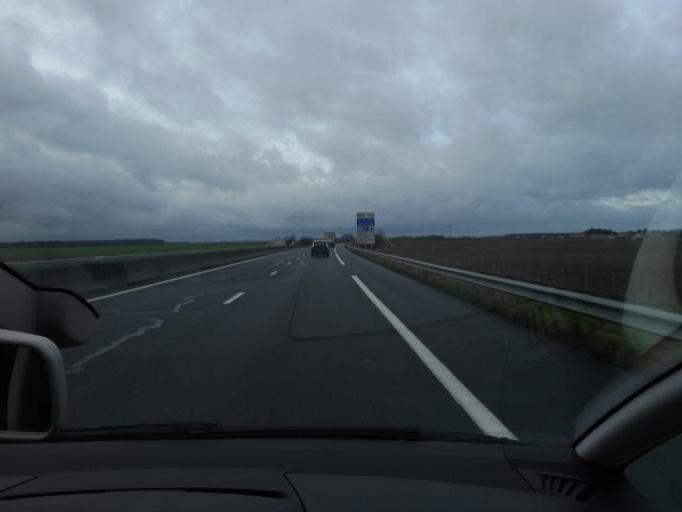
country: FR
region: Picardie
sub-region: Departement de la Somme
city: Villers-Bretonneux
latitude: 49.8556
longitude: 2.5401
